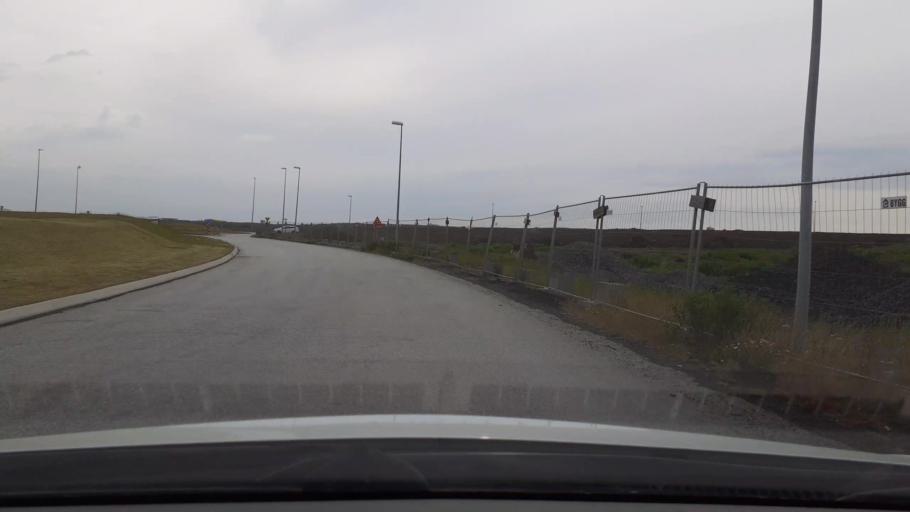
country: IS
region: Southern Peninsula
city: Reykjanesbaer
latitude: 63.9943
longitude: -22.5697
